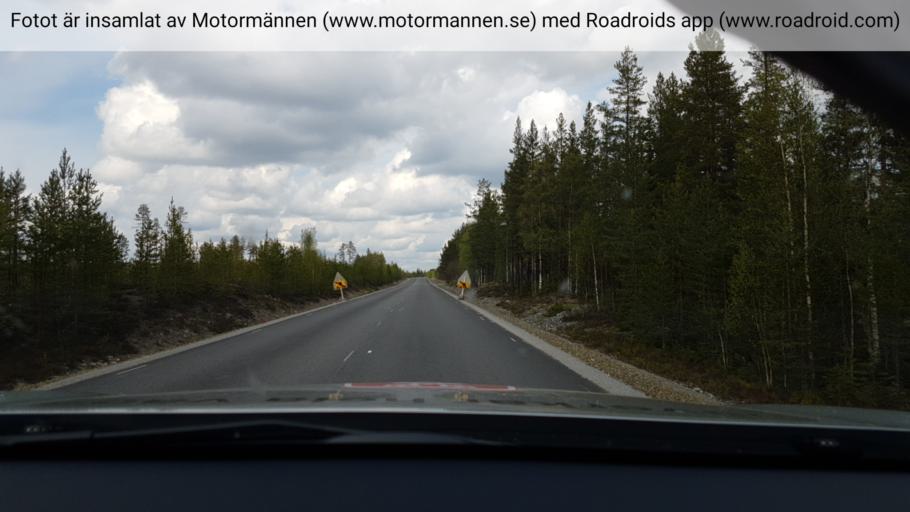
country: SE
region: Vaesterbotten
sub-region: Lycksele Kommun
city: Lycksele
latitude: 63.9802
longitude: 18.4877
